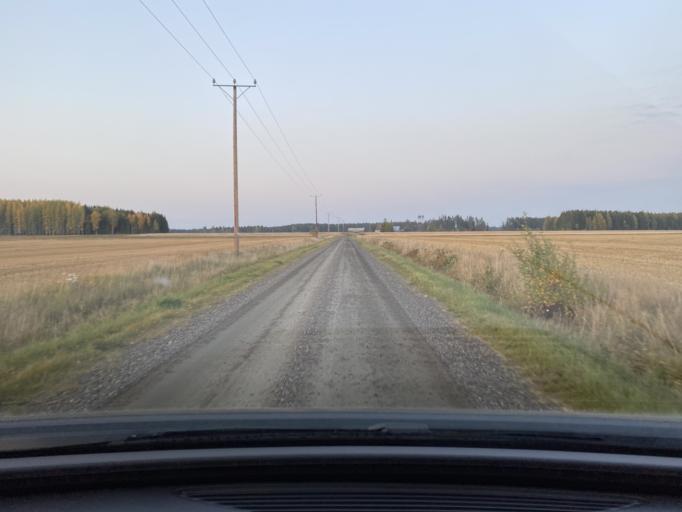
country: FI
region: Pirkanmaa
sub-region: Lounais-Pirkanmaa
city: Punkalaidun
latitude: 61.1029
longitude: 23.2121
